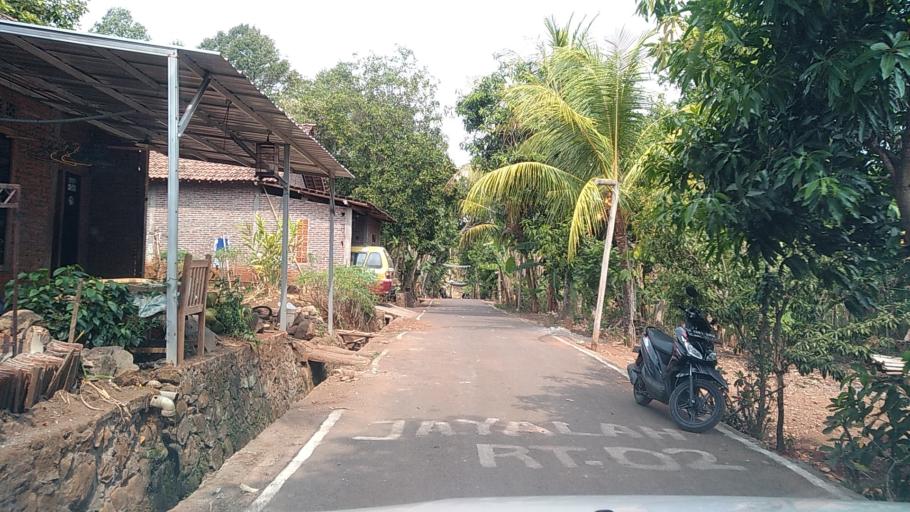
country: ID
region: Central Java
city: Semarang
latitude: -6.9990
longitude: 110.3095
